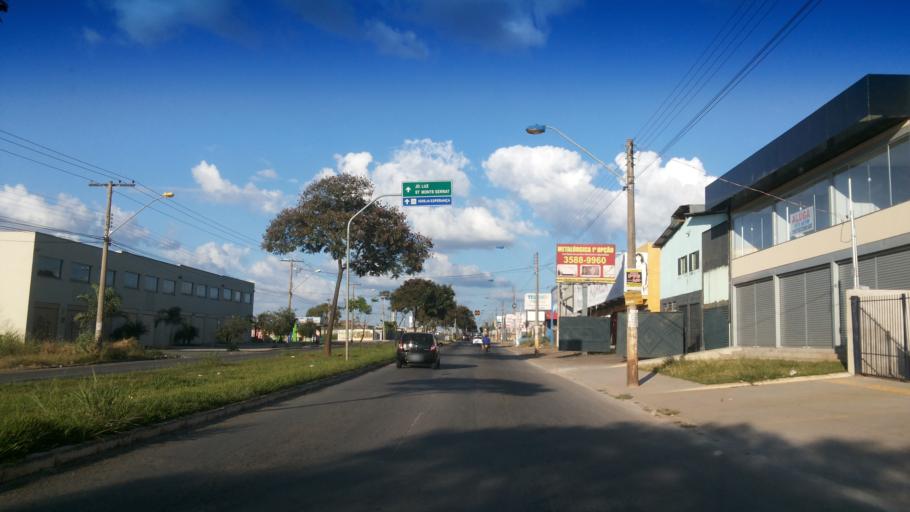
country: BR
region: Goias
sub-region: Goiania
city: Goiania
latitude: -16.7501
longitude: -49.3232
